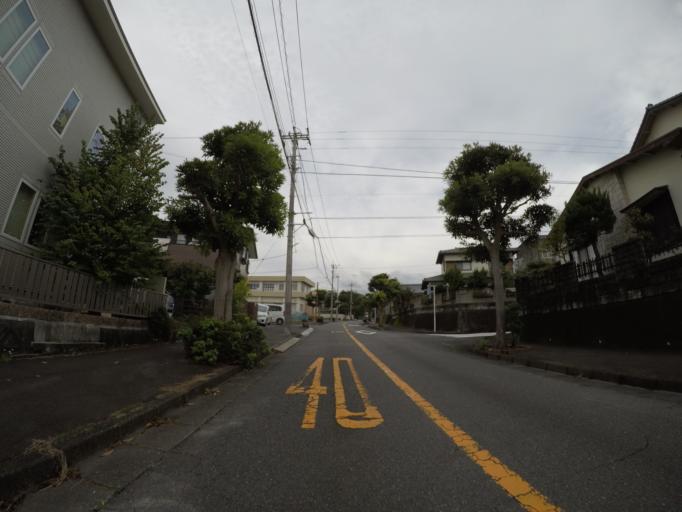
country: JP
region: Shizuoka
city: Fuji
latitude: 35.1842
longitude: 138.7078
